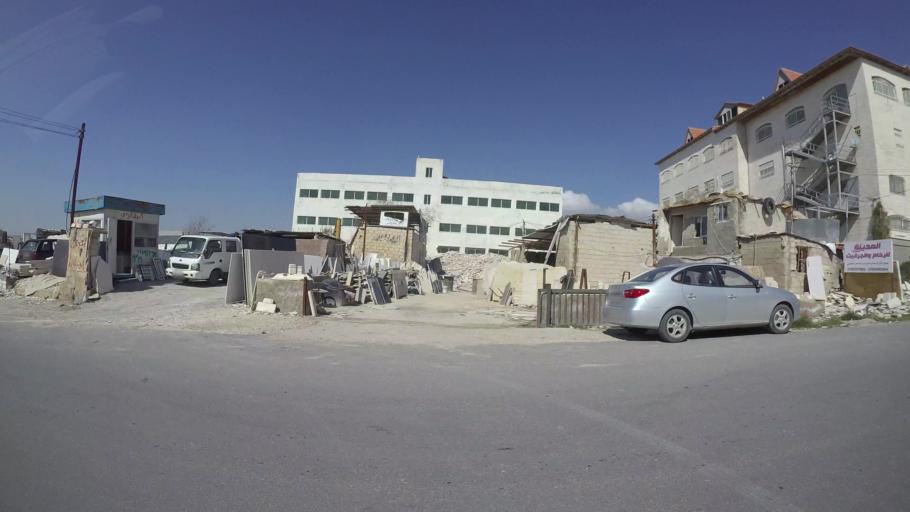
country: JO
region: Amman
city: Al Bunayyat ash Shamaliyah
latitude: 31.9112
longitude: 35.9114
